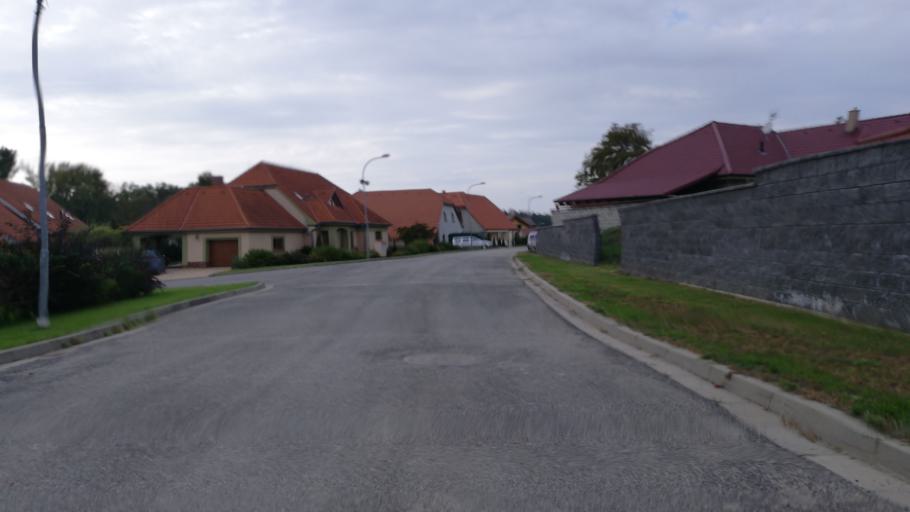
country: SK
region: Trnavsky
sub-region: Okres Skalica
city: Skalica
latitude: 48.8163
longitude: 17.2436
